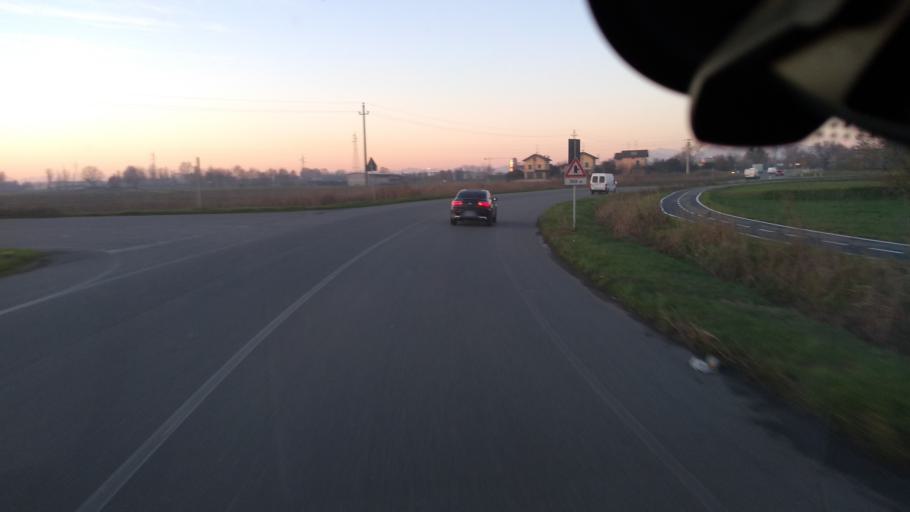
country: IT
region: Lombardy
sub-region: Provincia di Bergamo
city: Calvenzano
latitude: 45.5056
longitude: 9.5956
